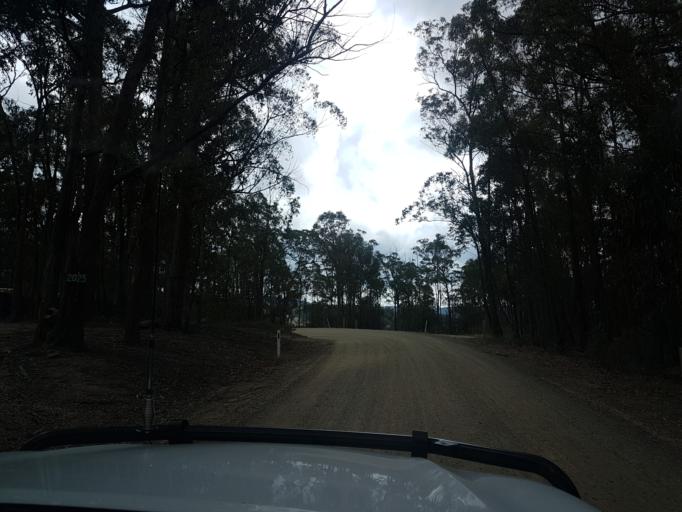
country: AU
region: Victoria
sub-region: East Gippsland
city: Bairnsdale
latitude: -37.6852
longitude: 147.5591
